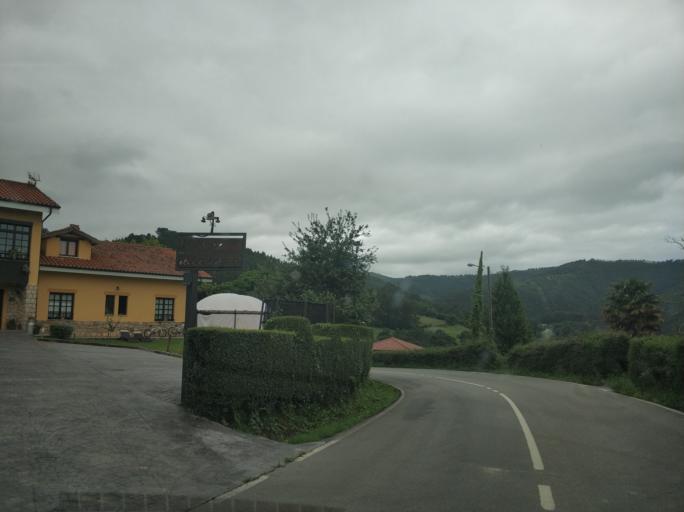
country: ES
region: Asturias
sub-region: Province of Asturias
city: Cudillero
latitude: 43.5427
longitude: -6.2428
